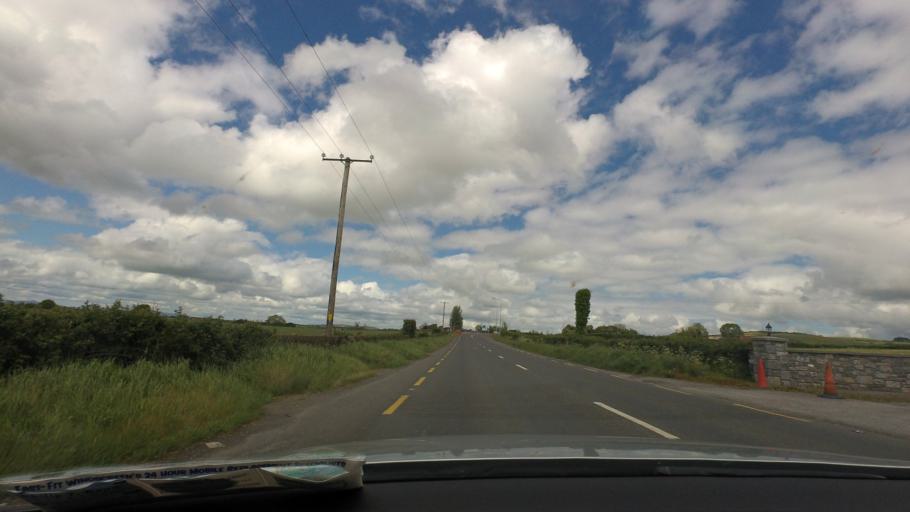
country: IE
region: Munster
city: Cashel
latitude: 52.5409
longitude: -7.8698
